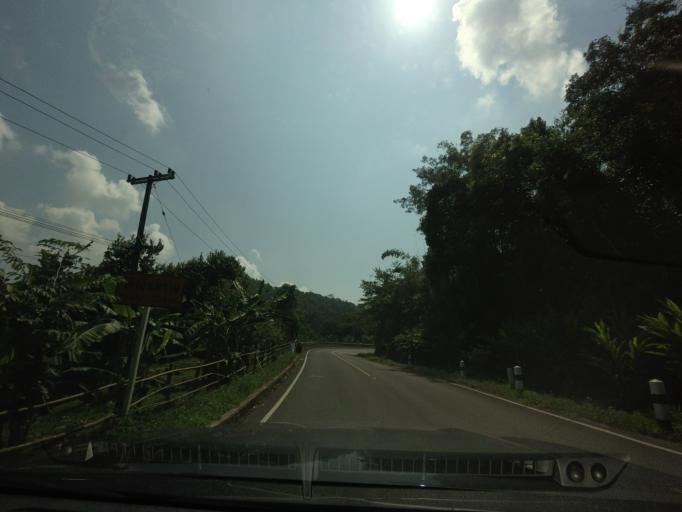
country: TH
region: Nan
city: Bo Kluea
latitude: 19.0428
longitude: 101.1704
